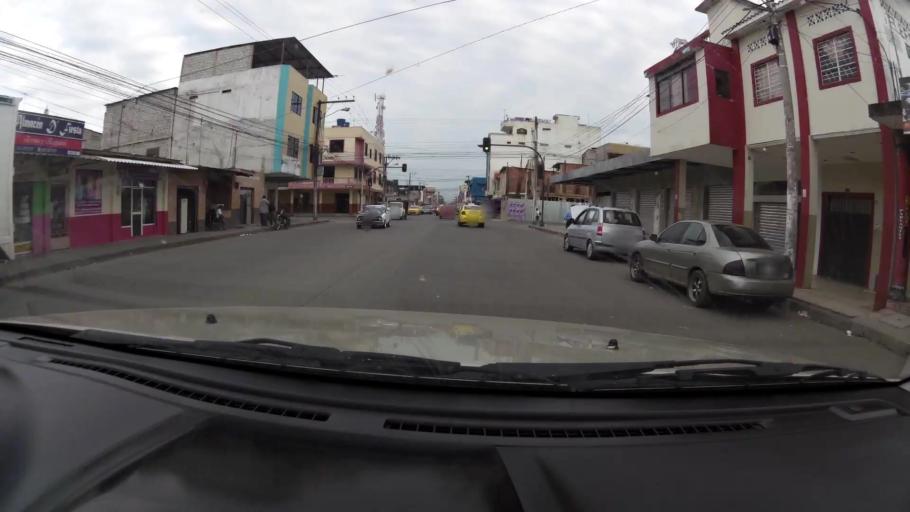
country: EC
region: El Oro
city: Machala
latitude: -3.2562
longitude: -79.9529
